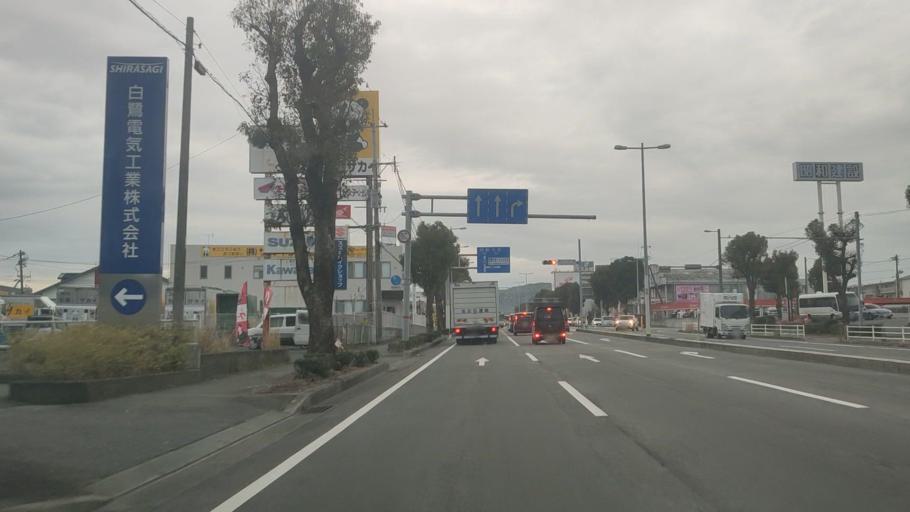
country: JP
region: Kumamoto
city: Kumamoto
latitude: 32.8297
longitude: 130.7703
